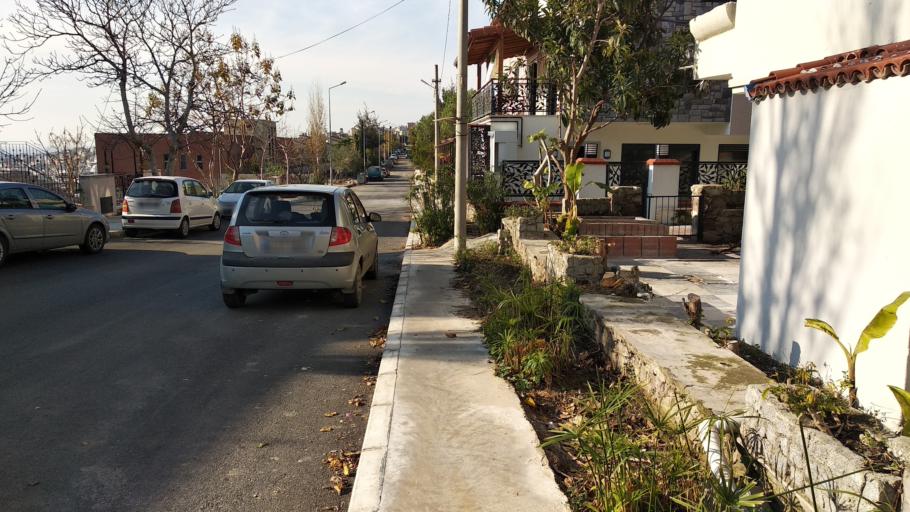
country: TR
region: Izmir
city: Karsiyaka
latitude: 38.4953
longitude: 27.0837
